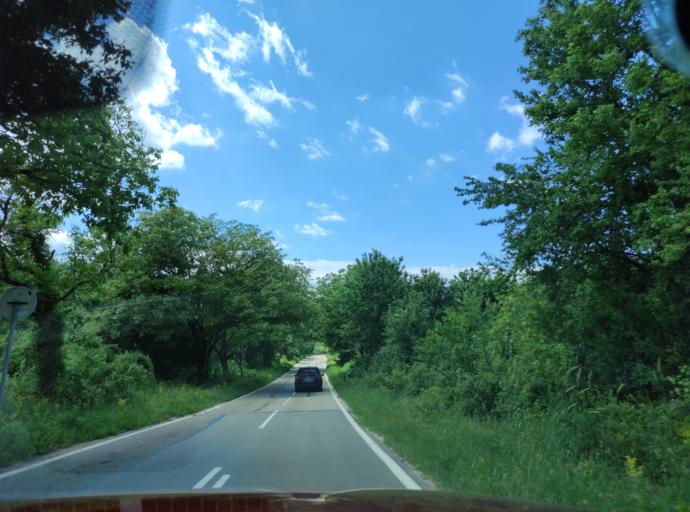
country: BG
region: Montana
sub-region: Obshtina Chiprovtsi
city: Chiprovtsi
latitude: 43.4831
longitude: 22.8244
